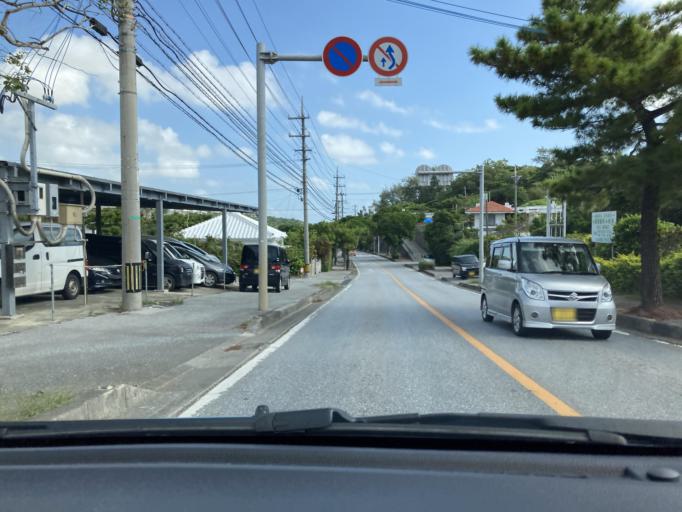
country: JP
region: Okinawa
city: Ginowan
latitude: 26.2683
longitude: 127.7771
